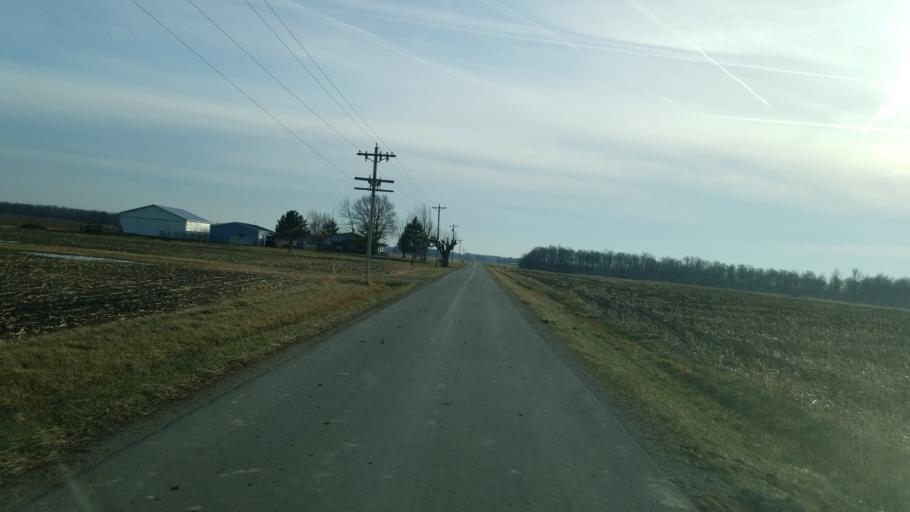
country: US
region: Ohio
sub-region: Hardin County
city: Forest
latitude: 40.7441
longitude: -83.4584
